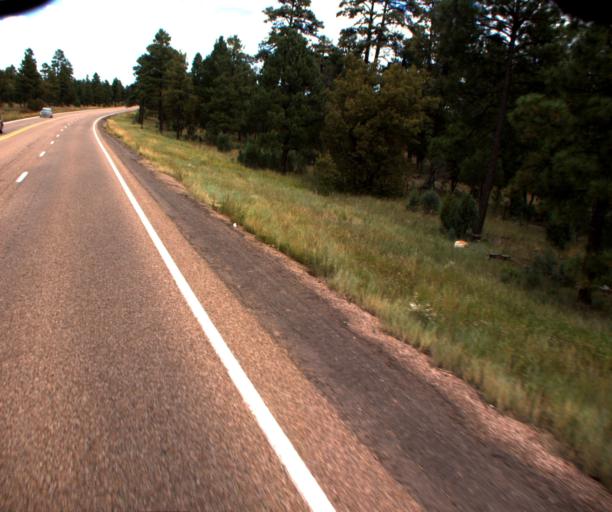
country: US
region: Arizona
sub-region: Navajo County
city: Heber-Overgaard
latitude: 34.4000
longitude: -110.6697
